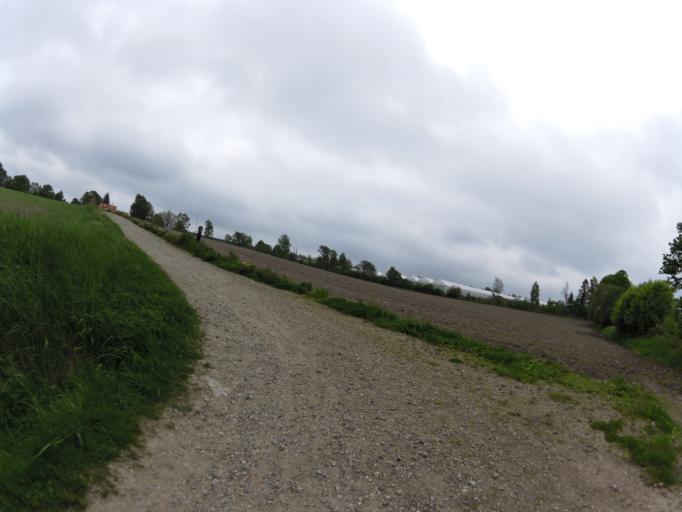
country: NO
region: Ostfold
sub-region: Moss
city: Moss
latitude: 59.3848
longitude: 10.6755
